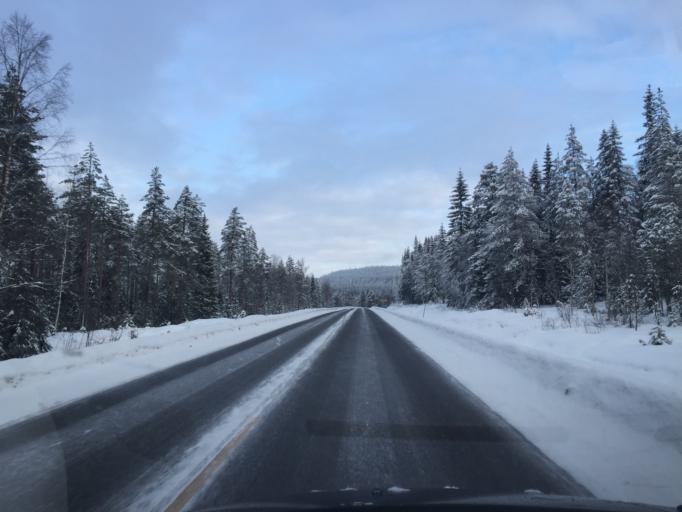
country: NO
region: Hedmark
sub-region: Elverum
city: Elverum
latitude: 61.0407
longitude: 11.8721
